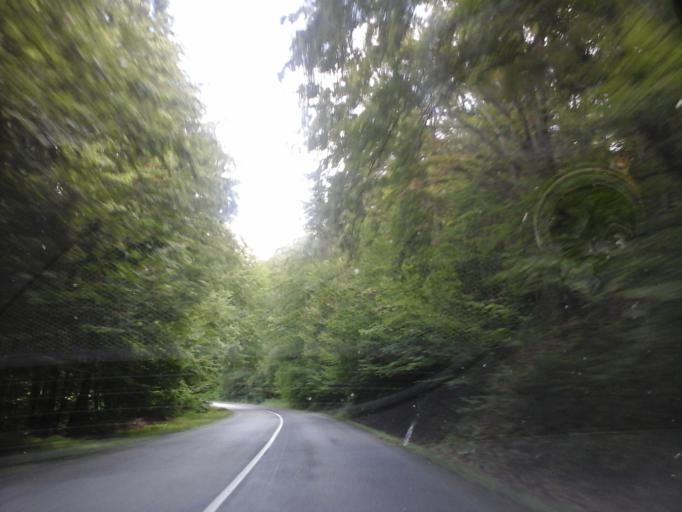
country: SK
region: Kosicky
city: Dobsina
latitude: 48.7111
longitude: 20.3749
